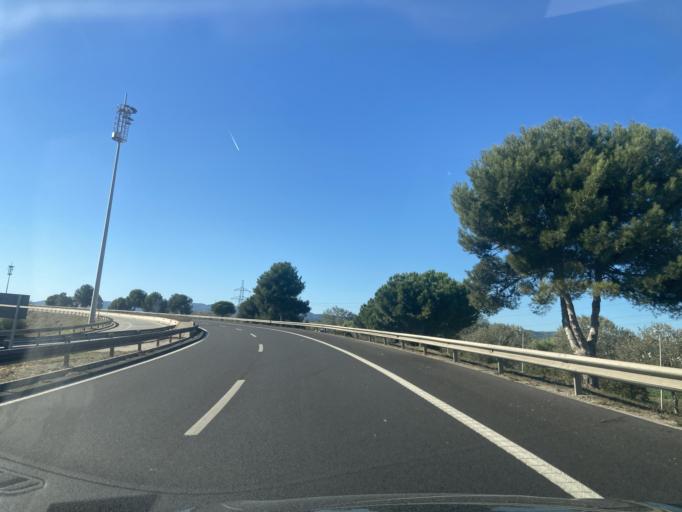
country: ES
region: Catalonia
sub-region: Provincia de Barcelona
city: Cornella de Llobregat
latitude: 41.3347
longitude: 2.0736
